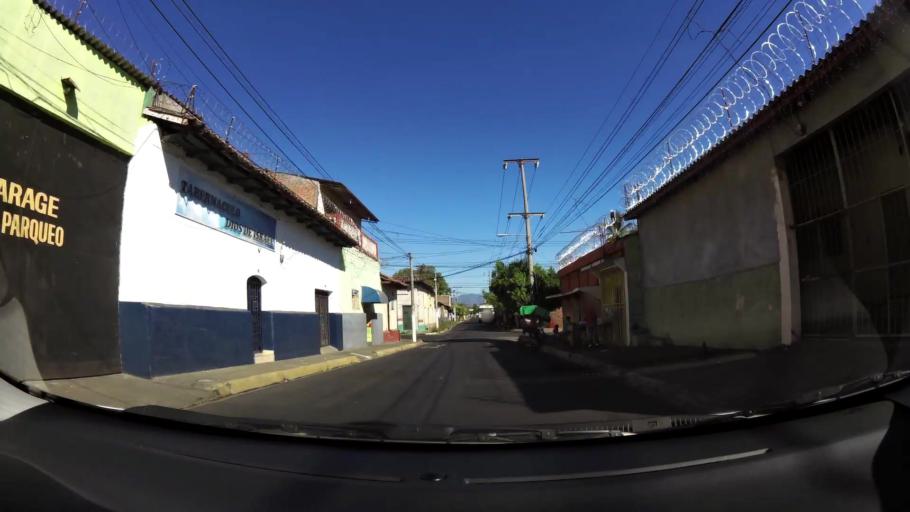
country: SV
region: San Miguel
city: San Miguel
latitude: 13.4874
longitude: -88.1768
